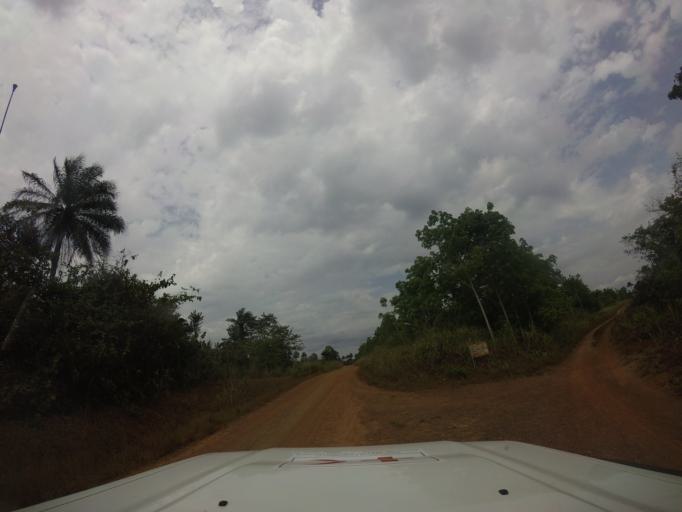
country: LR
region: Grand Cape Mount
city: Robertsport
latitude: 6.9346
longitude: -11.3392
